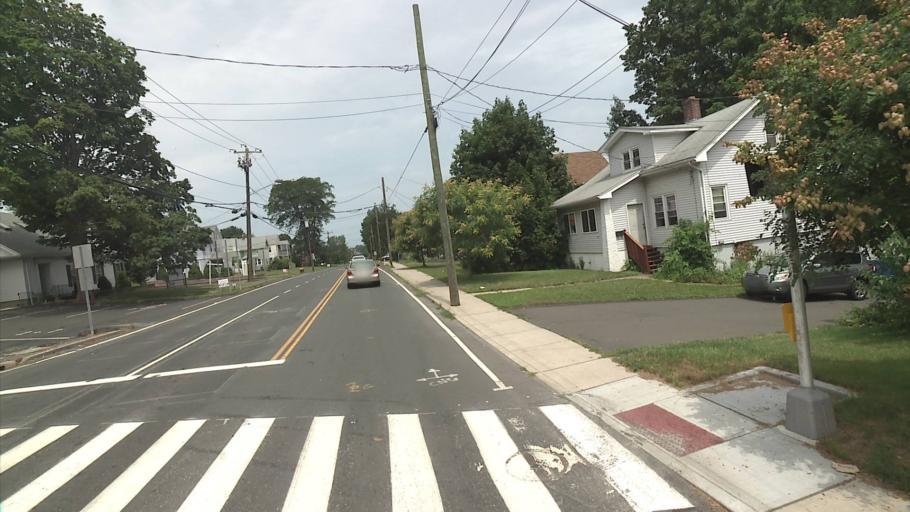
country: US
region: Connecticut
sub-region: Hartford County
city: Kensington
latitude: 41.6357
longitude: -72.7688
